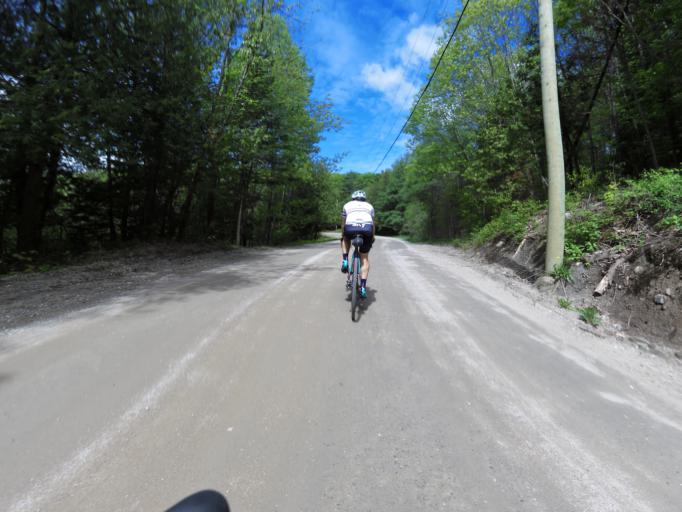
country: CA
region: Quebec
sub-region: Outaouais
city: Wakefield
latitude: 45.7864
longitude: -75.9750
